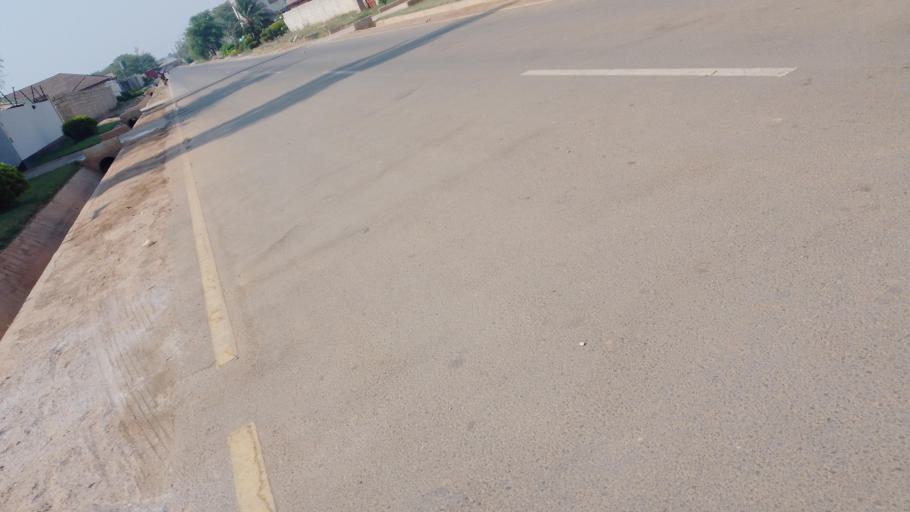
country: ZM
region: Lusaka
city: Lusaka
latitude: -15.3875
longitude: 28.3914
